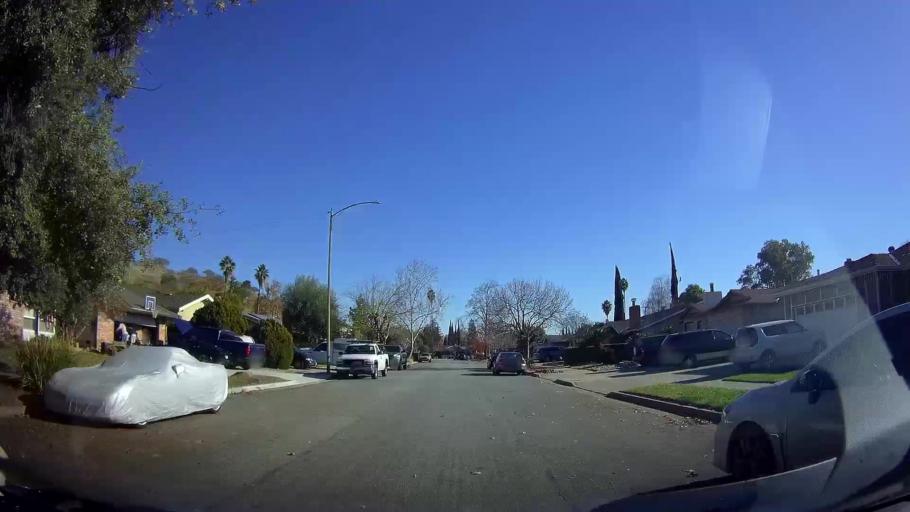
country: US
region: California
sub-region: Santa Clara County
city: Seven Trees
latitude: 37.2303
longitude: -121.8684
